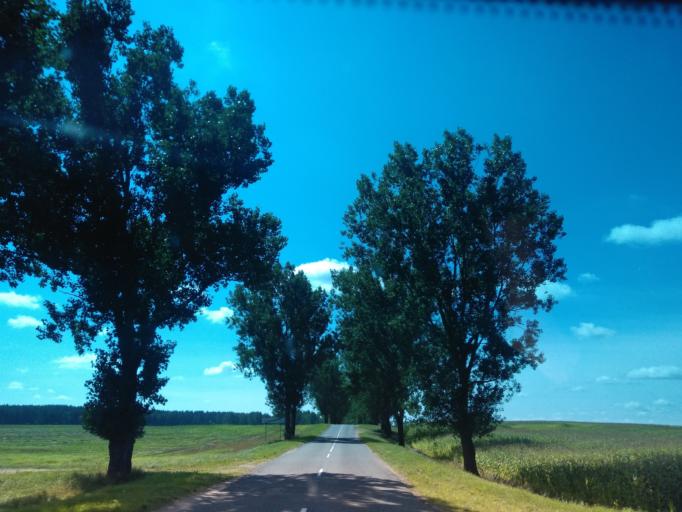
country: BY
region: Minsk
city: Uzda
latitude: 53.2835
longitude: 27.2313
